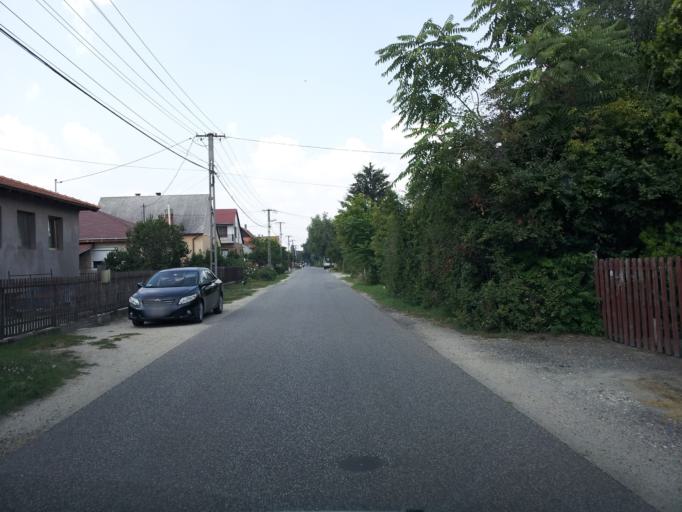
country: HU
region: Pest
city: Szigethalom
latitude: 47.3196
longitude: 19.0154
